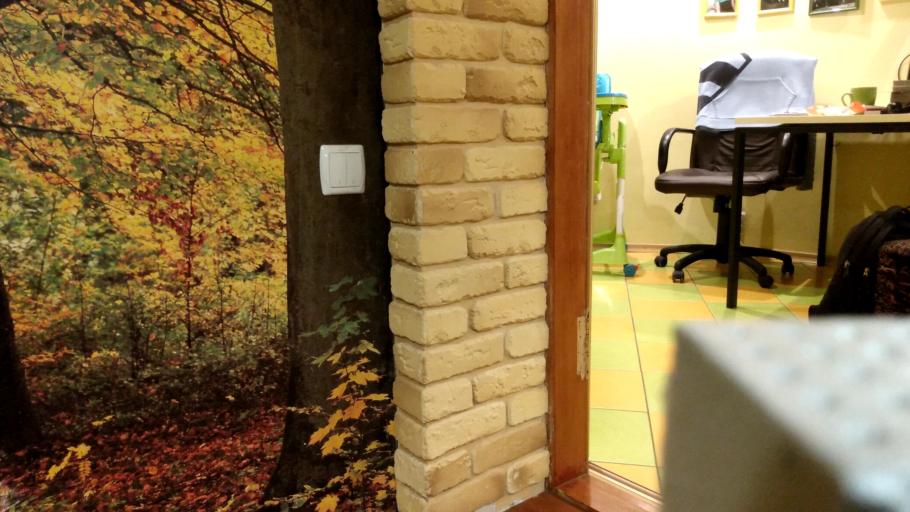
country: RU
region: Republic of Karelia
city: Pudozh
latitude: 61.6375
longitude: 37.7305
